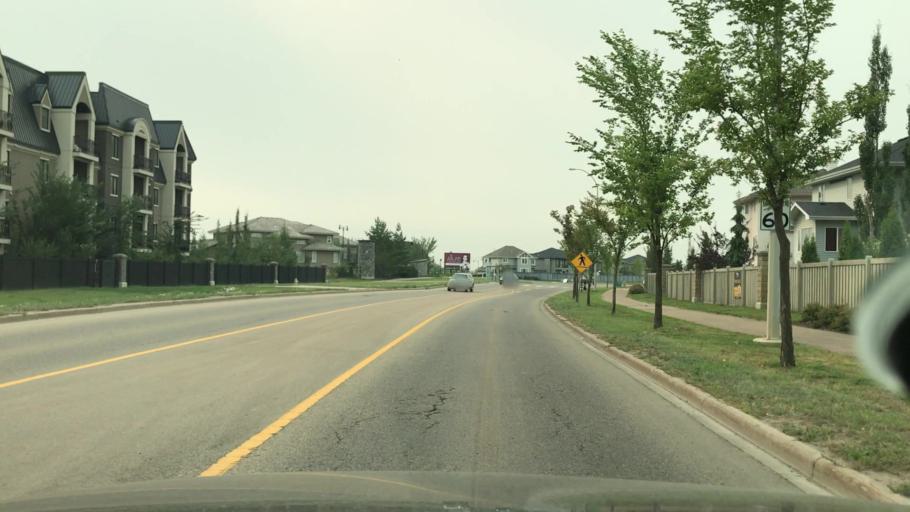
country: CA
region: Alberta
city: Edmonton
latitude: 53.4405
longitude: -113.5657
